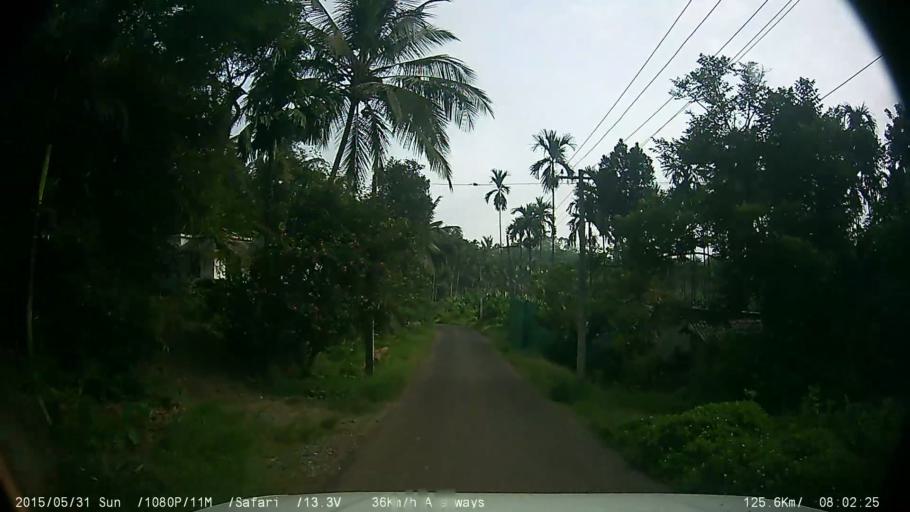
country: IN
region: Kerala
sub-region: Wayanad
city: Kalpetta
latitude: 11.6347
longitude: 76.0452
